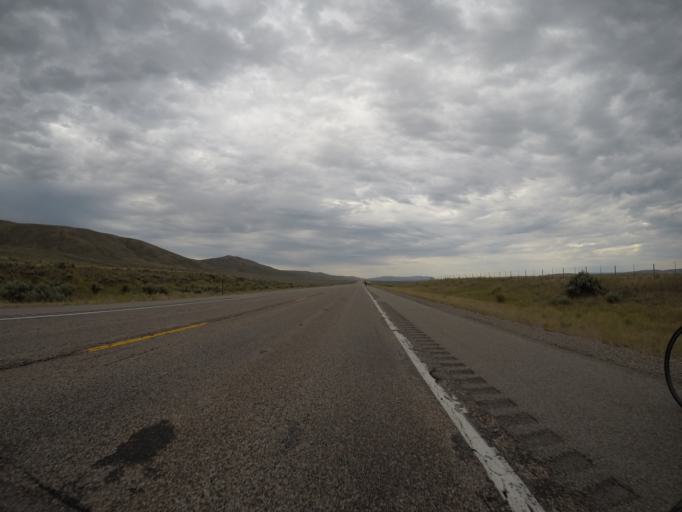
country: US
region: Utah
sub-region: Rich County
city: Randolph
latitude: 41.8716
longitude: -110.9675
